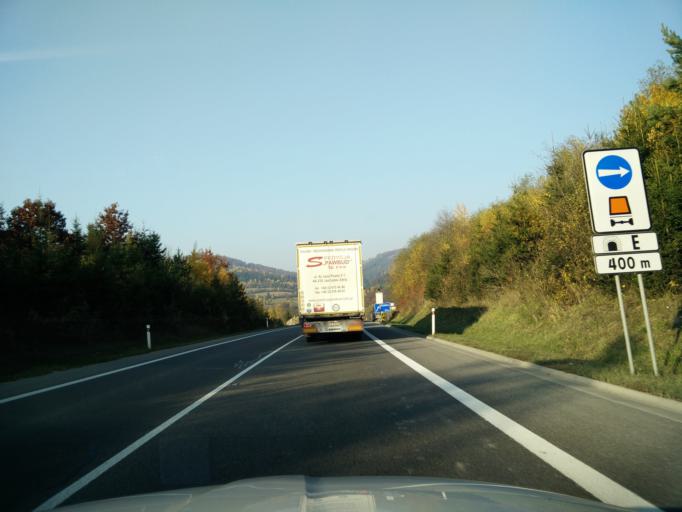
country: SK
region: Zilinsky
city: Cadca
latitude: 49.4174
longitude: 18.8378
